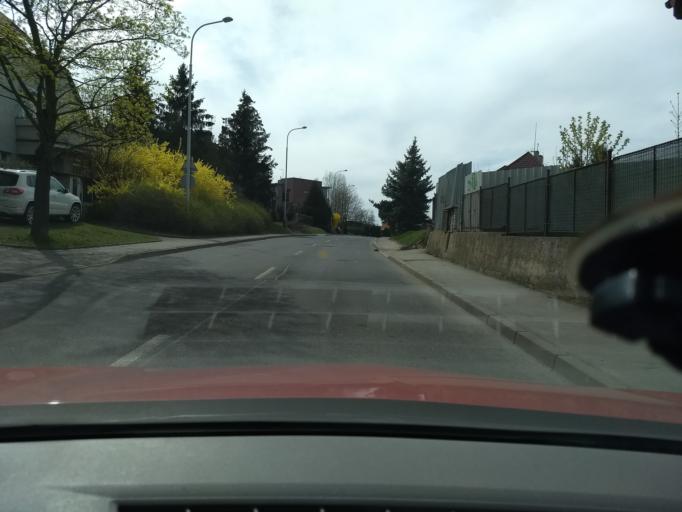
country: CZ
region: Central Bohemia
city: Hostivice
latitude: 50.0681
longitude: 14.2944
